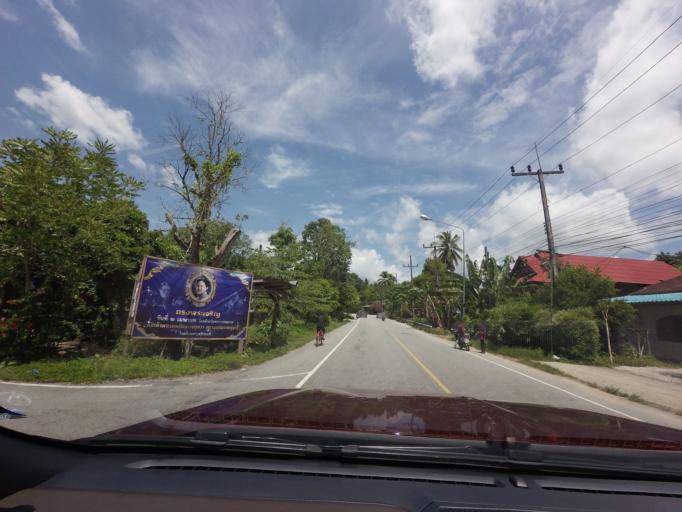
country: TH
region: Narathiwat
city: Ra-ngae
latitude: 6.2525
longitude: 101.6852
